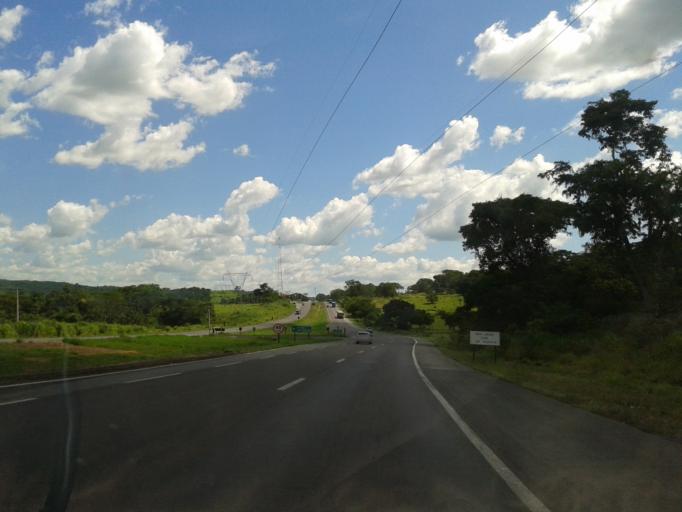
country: BR
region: Goias
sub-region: Piracanjuba
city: Piracanjuba
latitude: -17.4045
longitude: -49.2241
